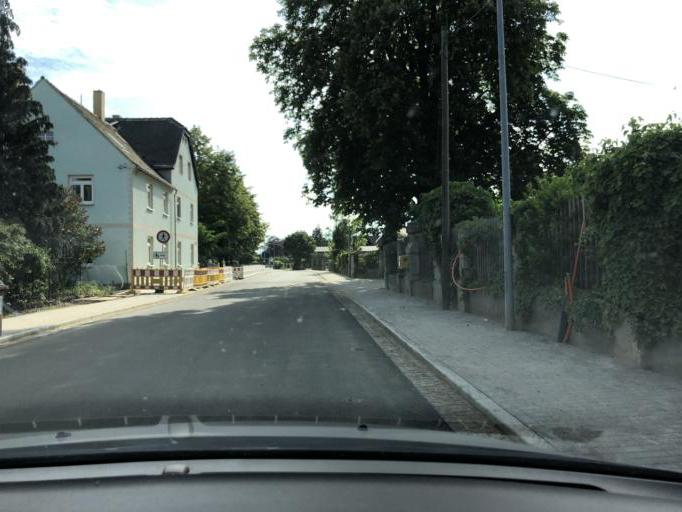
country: DE
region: Saxony
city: Borsdorf
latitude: 51.3220
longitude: 12.5543
